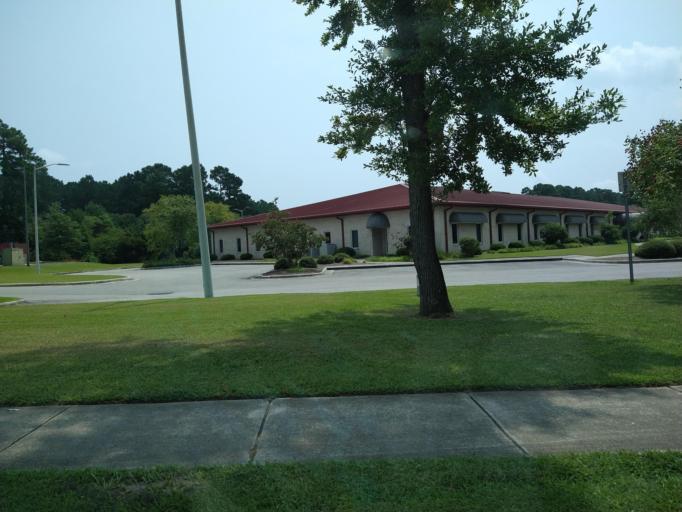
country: US
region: North Carolina
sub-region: Onslow County
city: Pumpkin Center
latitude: 34.7607
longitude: -77.3772
